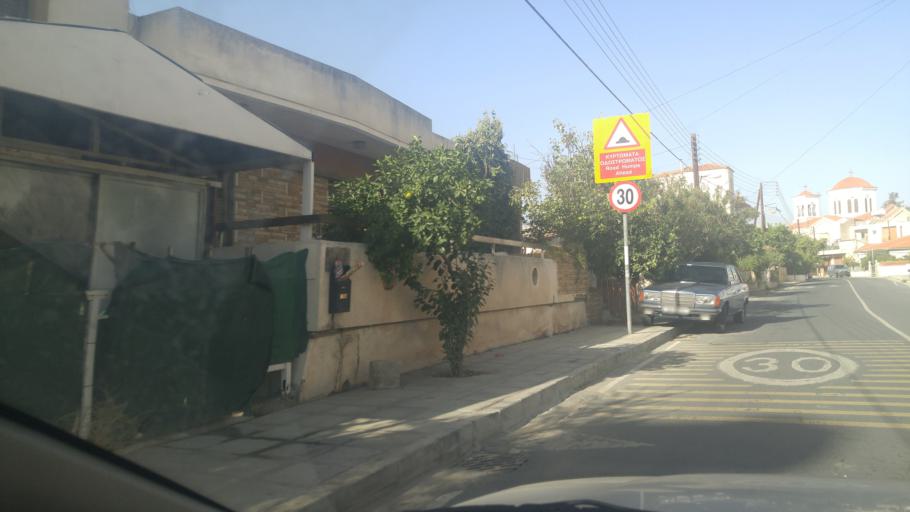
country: CY
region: Limassol
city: Pano Polemidia
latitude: 34.6927
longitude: 33.0022
